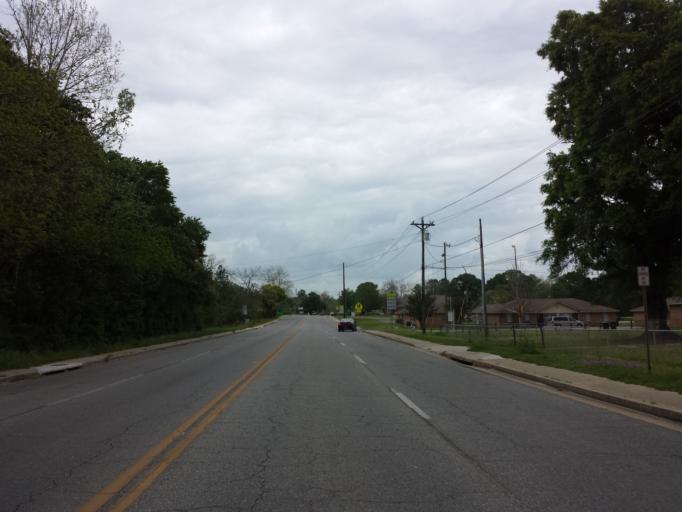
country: US
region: Georgia
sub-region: Tift County
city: Unionville
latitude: 31.4341
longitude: -83.5170
